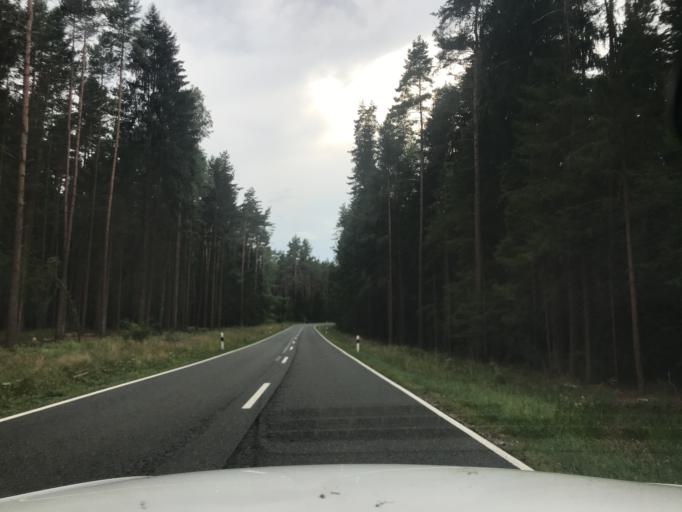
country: DE
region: Bavaria
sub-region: Upper Franconia
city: Pegnitz
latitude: 49.7340
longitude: 11.4733
